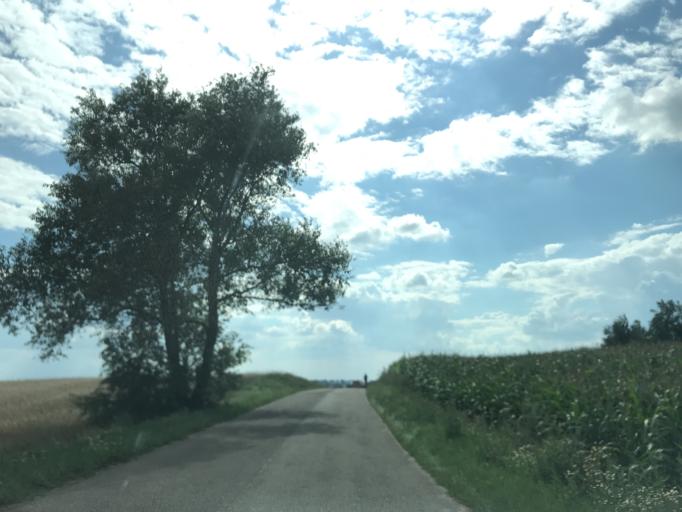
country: PL
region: Kujawsko-Pomorskie
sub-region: Powiat brodnicki
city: Brzozie
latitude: 53.3377
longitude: 19.6641
